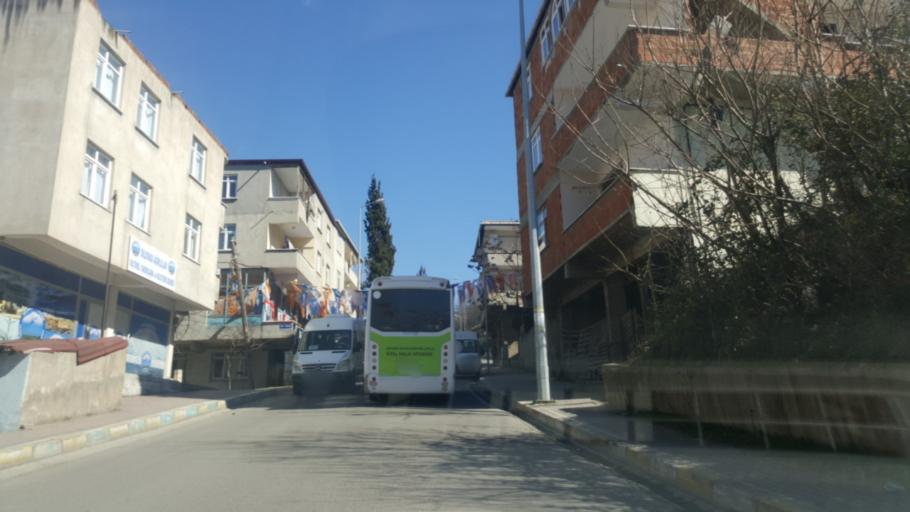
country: TR
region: Kocaeli
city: Tavsancil
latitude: 40.7856
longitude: 29.5490
